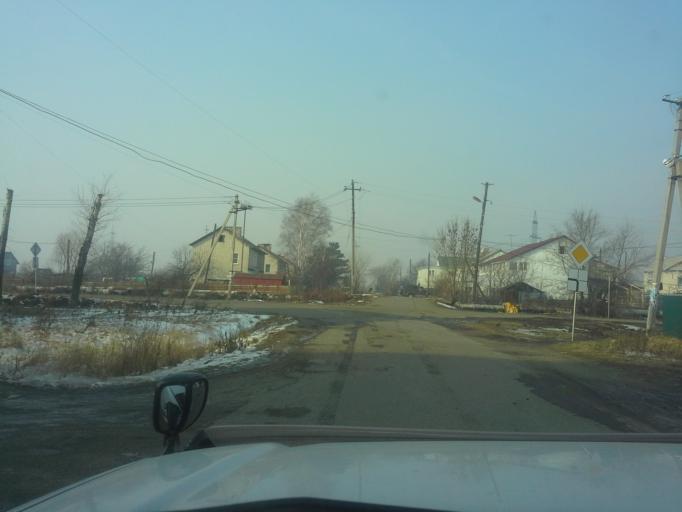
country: RU
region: Jewish Autonomous Oblast
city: Priamurskiy
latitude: 48.5291
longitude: 134.9002
